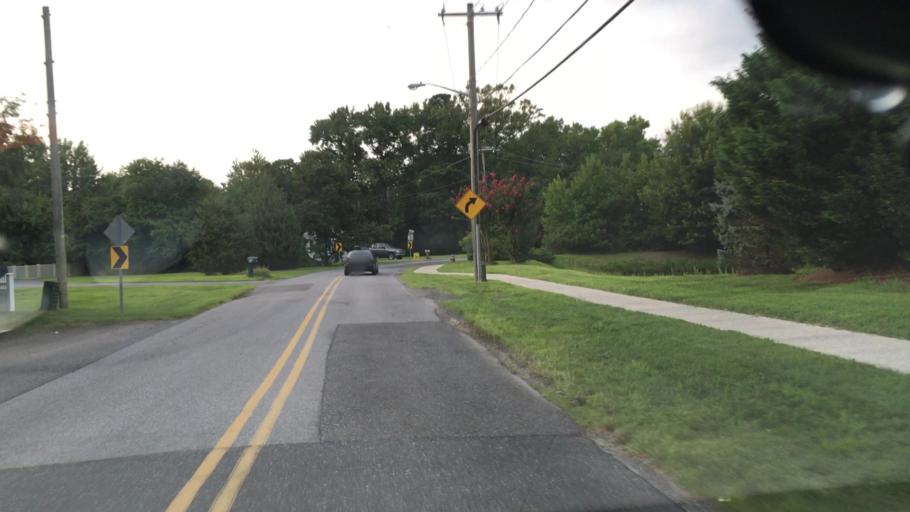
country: US
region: Delaware
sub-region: Sussex County
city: Ocean View
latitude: 38.5406
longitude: -75.0957
